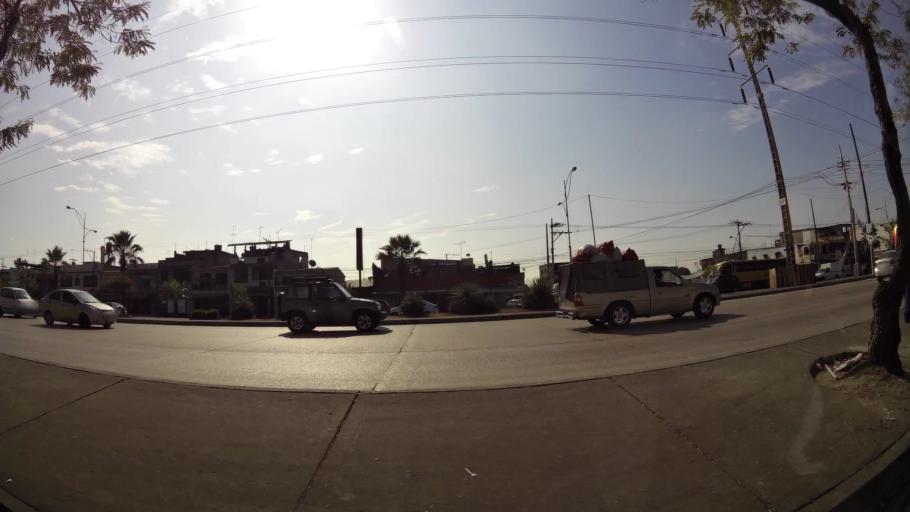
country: EC
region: Guayas
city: Eloy Alfaro
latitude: -2.0874
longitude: -79.9141
